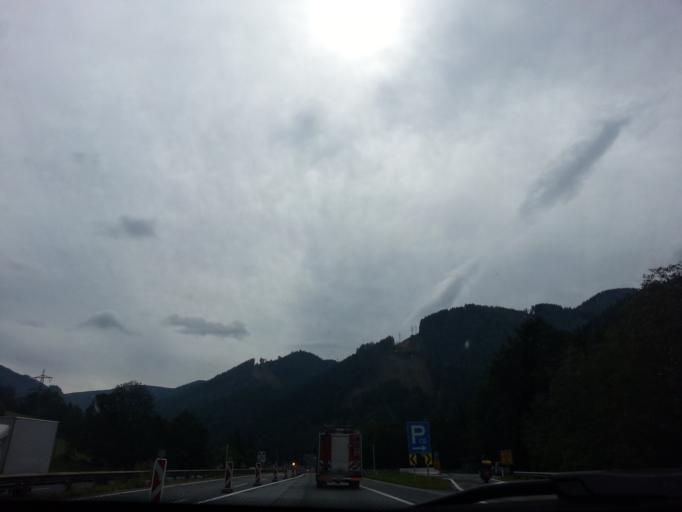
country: AT
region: Styria
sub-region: Politischer Bezirk Leoben
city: Sankt Michael in Obersteiermark
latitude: 47.2983
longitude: 15.0716
